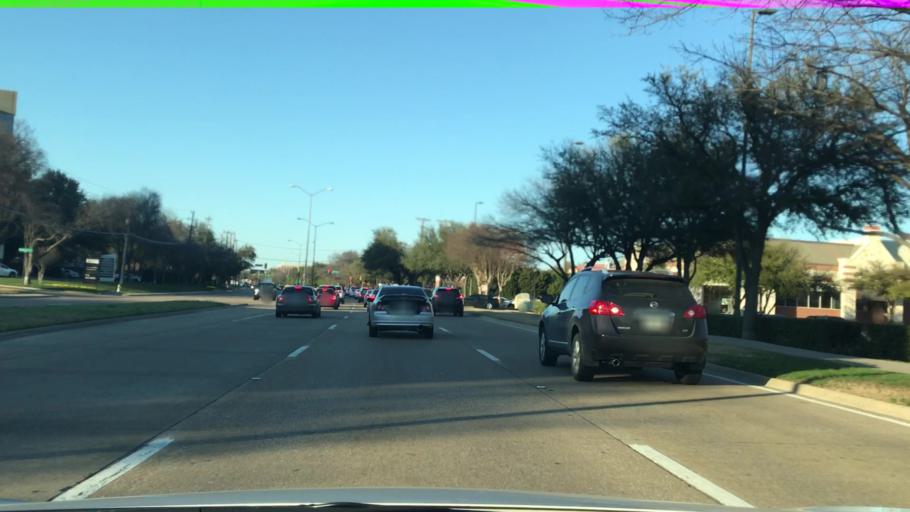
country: US
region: Texas
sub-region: Dallas County
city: Addison
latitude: 33.0005
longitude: -96.7966
